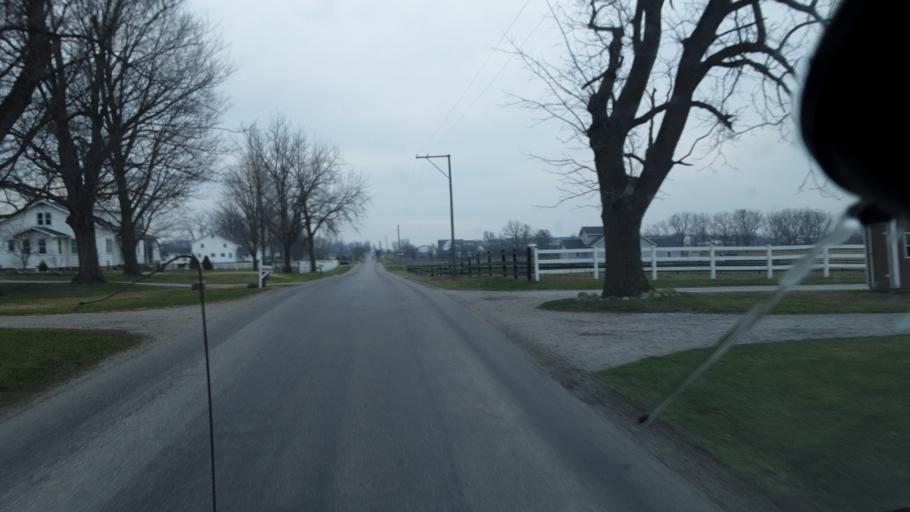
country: US
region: Indiana
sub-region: Elkhart County
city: Middlebury
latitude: 41.6836
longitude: -85.6197
